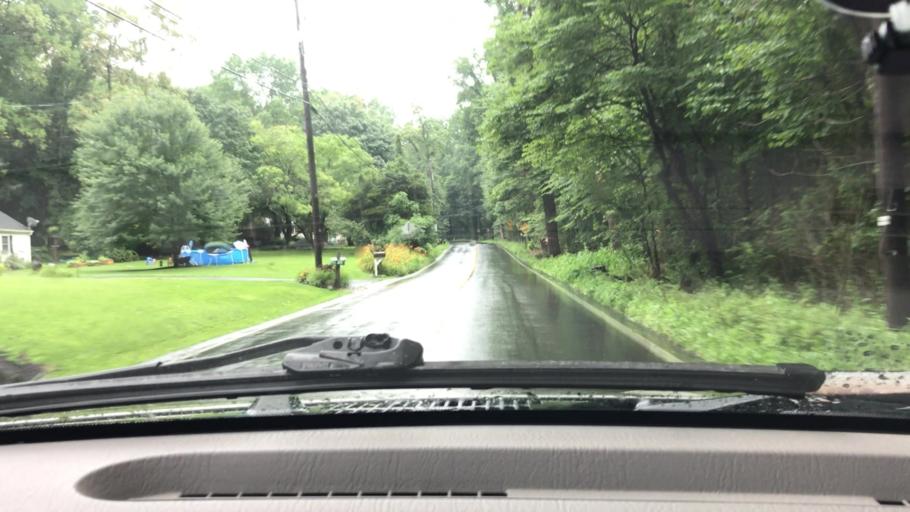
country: US
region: Pennsylvania
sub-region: Lancaster County
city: Elizabethtown
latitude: 40.1850
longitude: -76.5865
